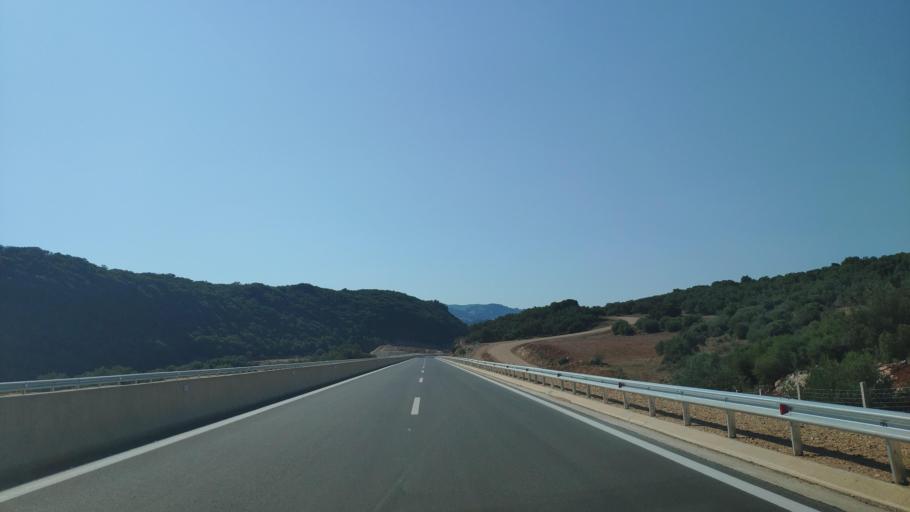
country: GR
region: West Greece
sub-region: Nomos Aitolias kai Akarnanias
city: Stanos
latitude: 38.7791
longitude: 21.1497
